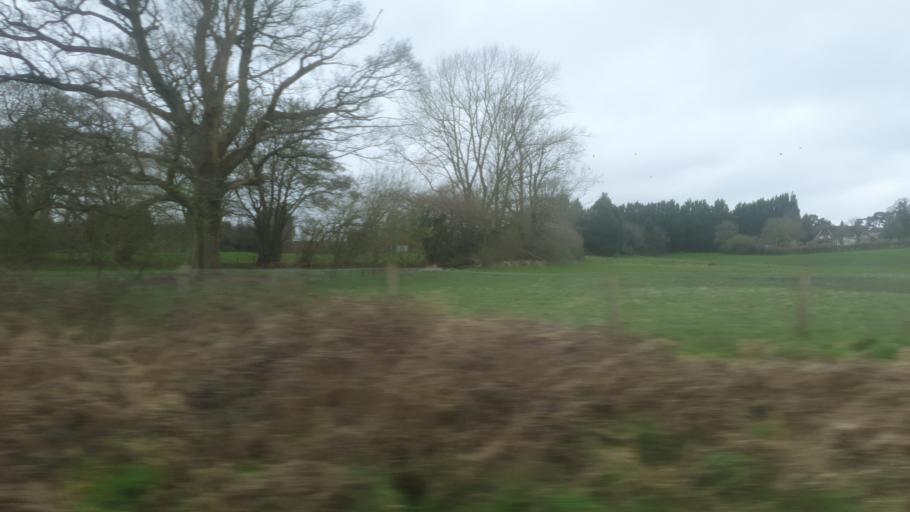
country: GB
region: England
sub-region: West Sussex
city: Pulborough
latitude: 50.9667
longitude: -0.4963
